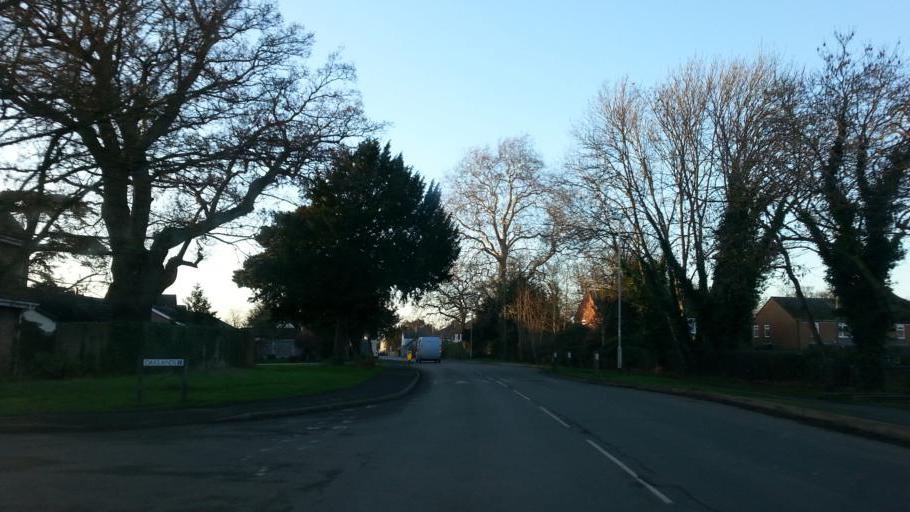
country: GB
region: England
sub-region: Cambridgeshire
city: Hemingford Grey
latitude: 52.2971
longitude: -0.0670
